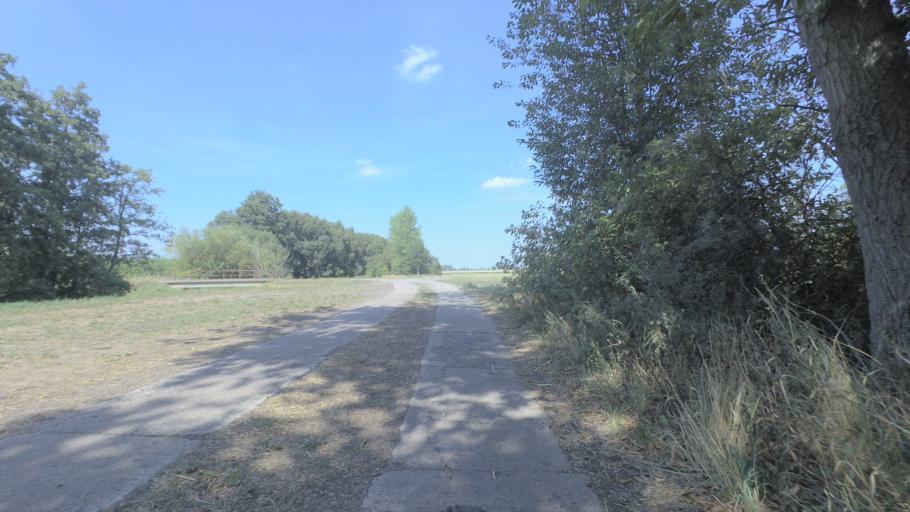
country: DE
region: Brandenburg
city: Trebbin
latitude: 52.1821
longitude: 13.2651
